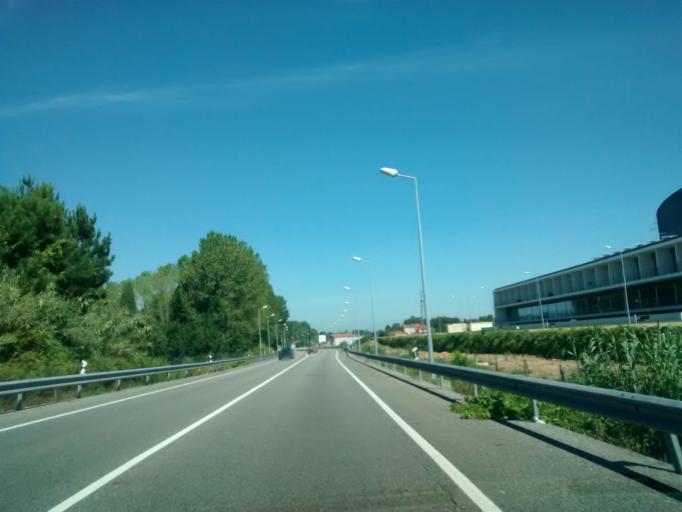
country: PT
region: Aveiro
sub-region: Anadia
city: Sangalhos
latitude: 40.4784
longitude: -8.4763
